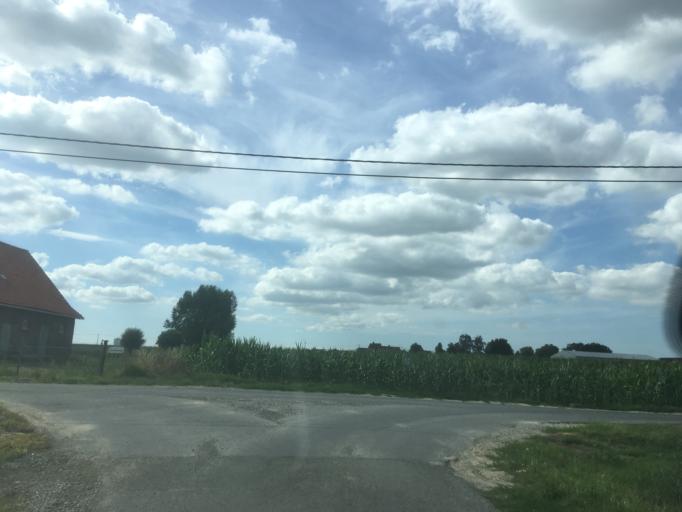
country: BE
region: Flanders
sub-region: Provincie West-Vlaanderen
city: Moorslede
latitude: 50.9050
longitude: 3.0775
